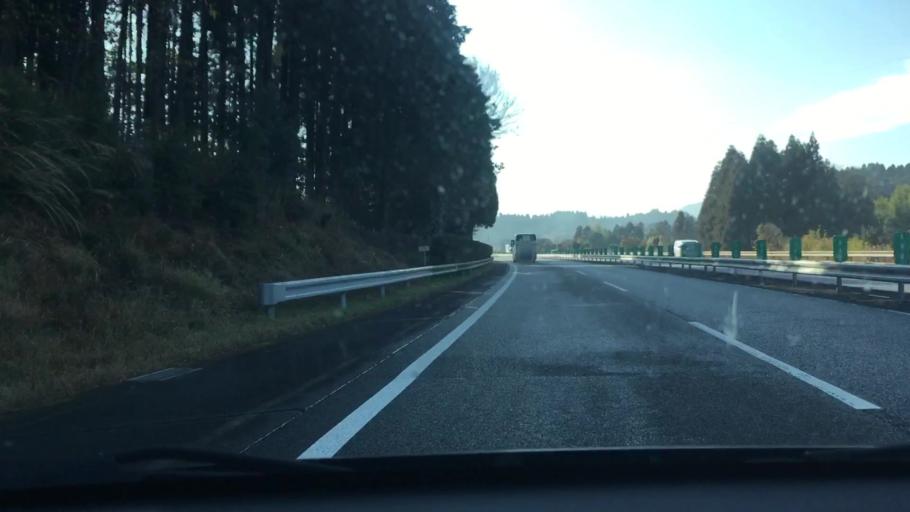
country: JP
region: Kagoshima
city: Okuchi-shinohara
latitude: 32.0231
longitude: 130.7784
